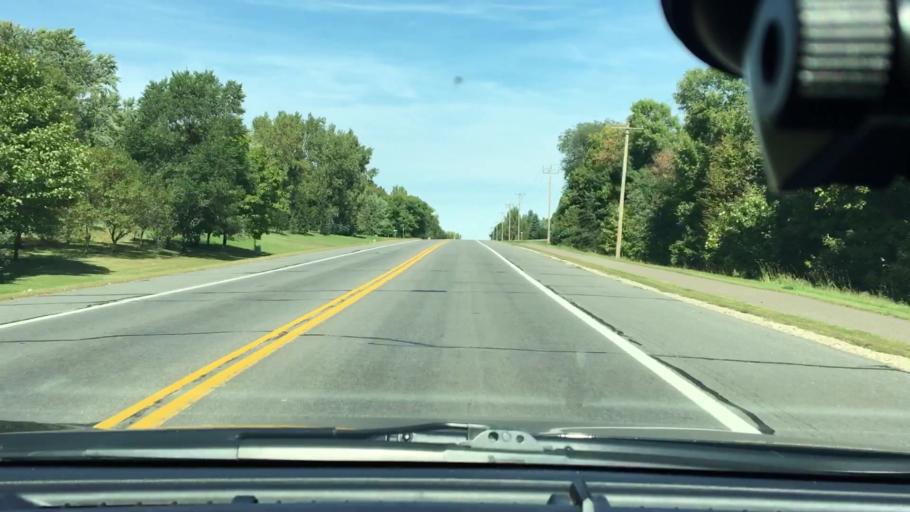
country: US
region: Minnesota
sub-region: Wright County
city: Hanover
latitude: 45.1641
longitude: -93.6659
